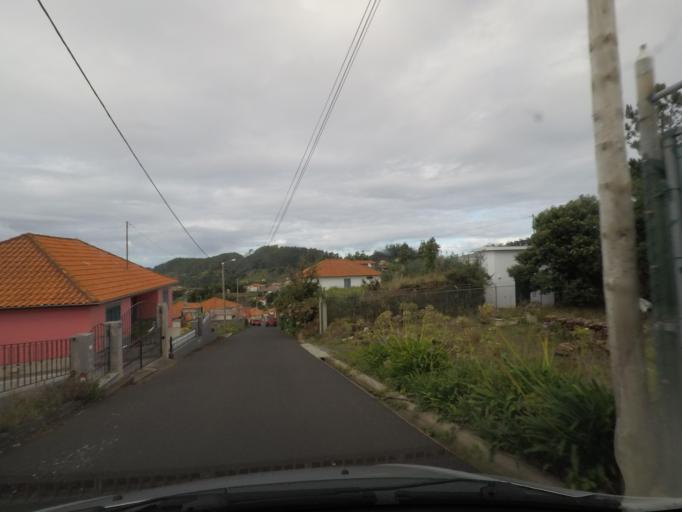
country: PT
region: Madeira
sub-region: Santana
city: Santana
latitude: 32.7937
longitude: -16.8765
